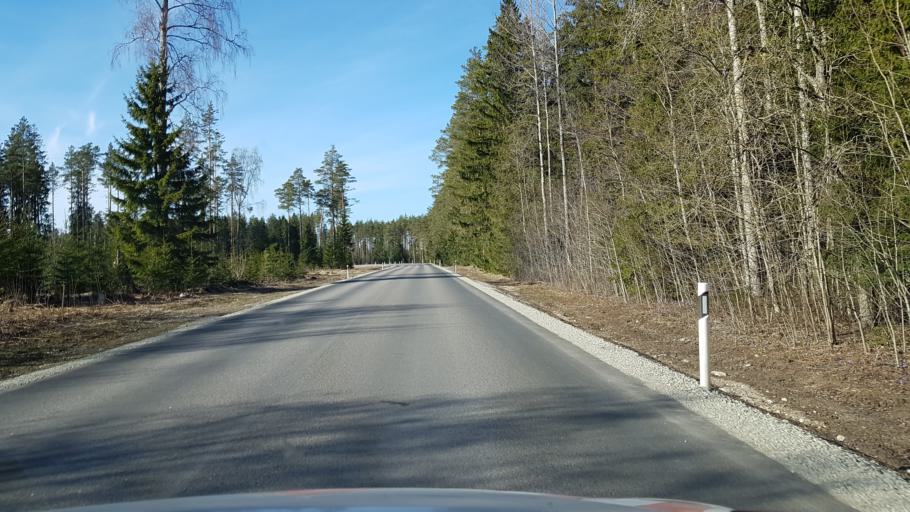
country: EE
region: Laeaene-Virumaa
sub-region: Vinni vald
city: Vinni
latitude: 59.1223
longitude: 26.6173
